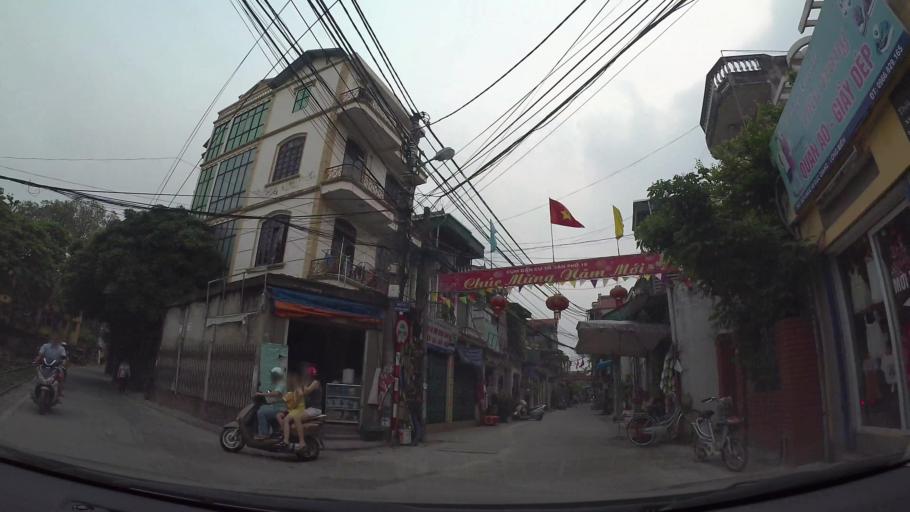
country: VN
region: Ha Noi
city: Hoan Kiem
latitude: 21.0642
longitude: 105.8927
